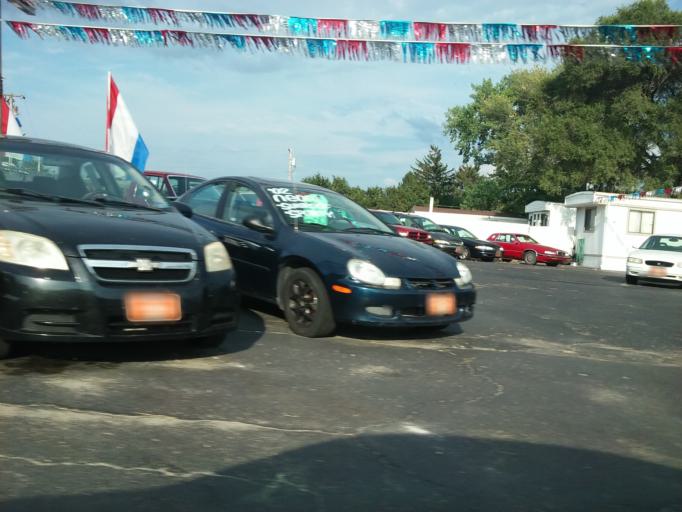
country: US
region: Ohio
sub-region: Wood County
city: Bowling Green
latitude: 41.3630
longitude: -83.6504
